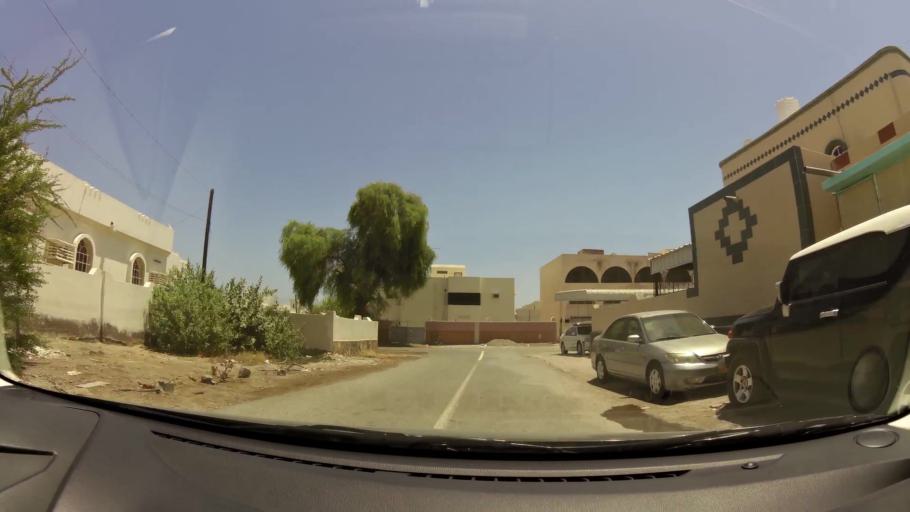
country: OM
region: Muhafazat Masqat
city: As Sib al Jadidah
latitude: 23.6329
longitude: 58.2429
